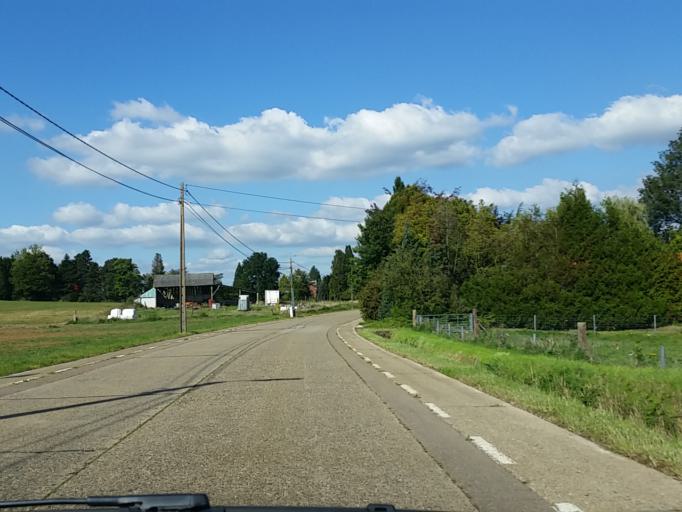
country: BE
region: Flanders
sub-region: Provincie Vlaams-Brabant
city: Lubbeek
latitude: 50.9120
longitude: 4.8418
